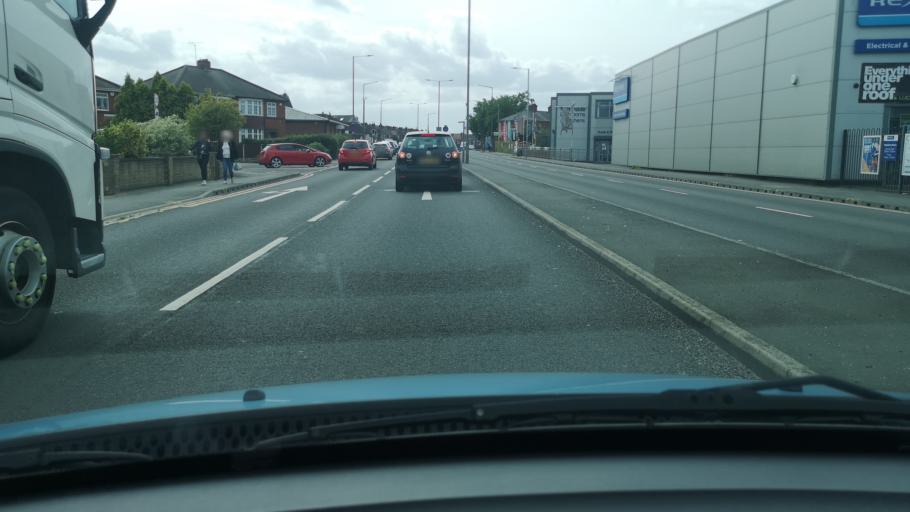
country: GB
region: England
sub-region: Doncaster
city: Doncaster
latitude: 53.5347
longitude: -1.1224
